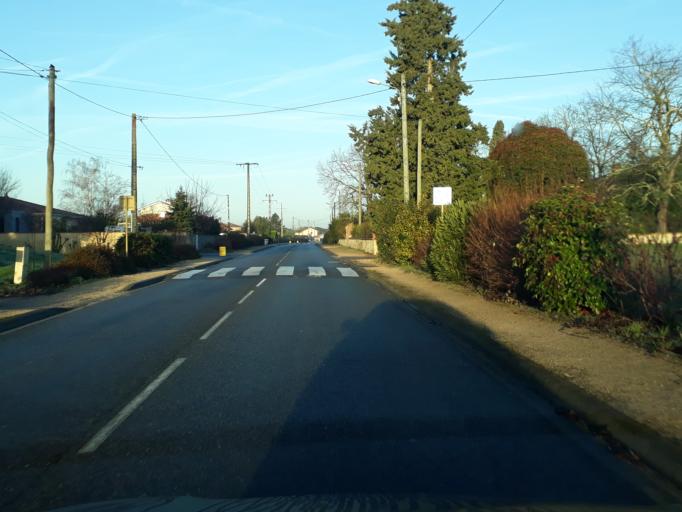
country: FR
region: Midi-Pyrenees
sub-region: Departement de la Haute-Garonne
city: Longages
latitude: 43.3566
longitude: 1.2333
